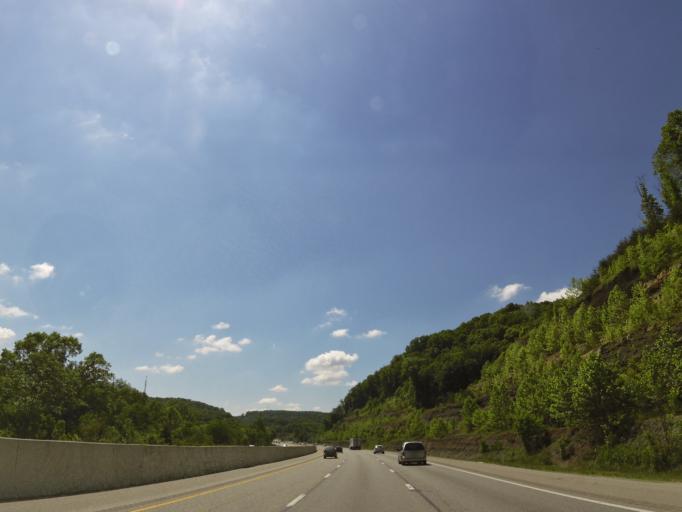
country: US
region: Kentucky
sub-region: Rockcastle County
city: Mount Vernon
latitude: 37.2450
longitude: -84.2447
